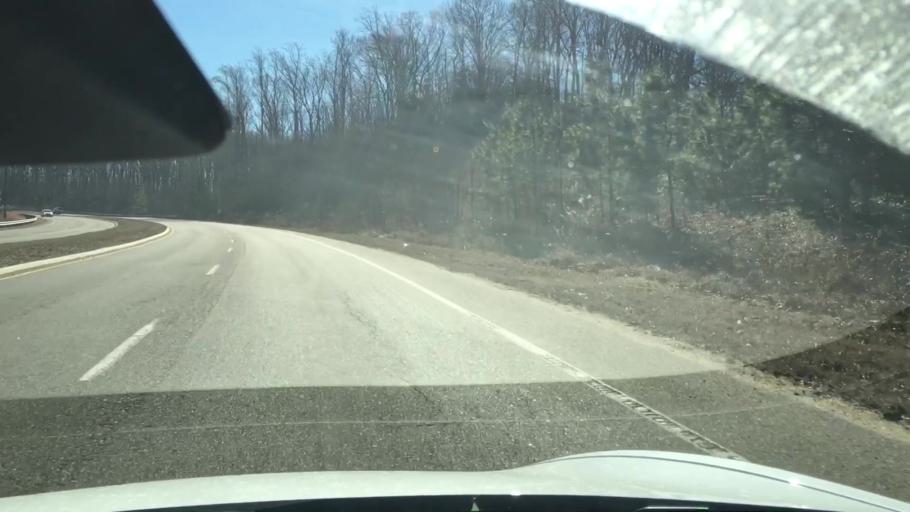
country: US
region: Virginia
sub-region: Chesterfield County
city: Bon Air
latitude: 37.5448
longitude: -77.6521
